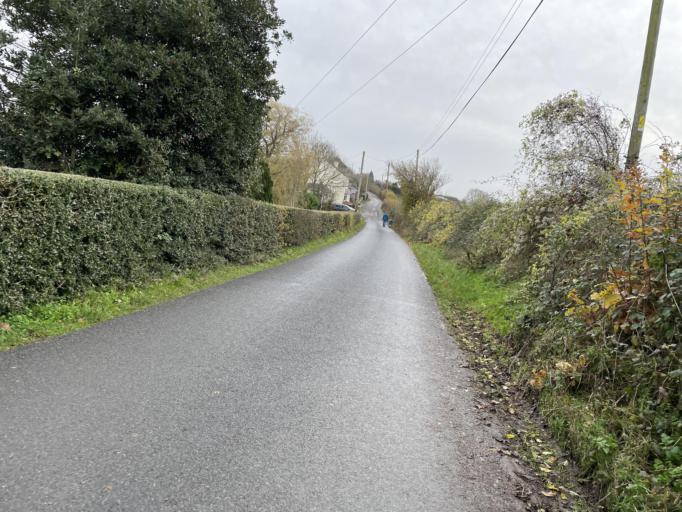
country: GB
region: England
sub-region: Herefordshire
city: Linton
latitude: 51.9199
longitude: -2.4882
